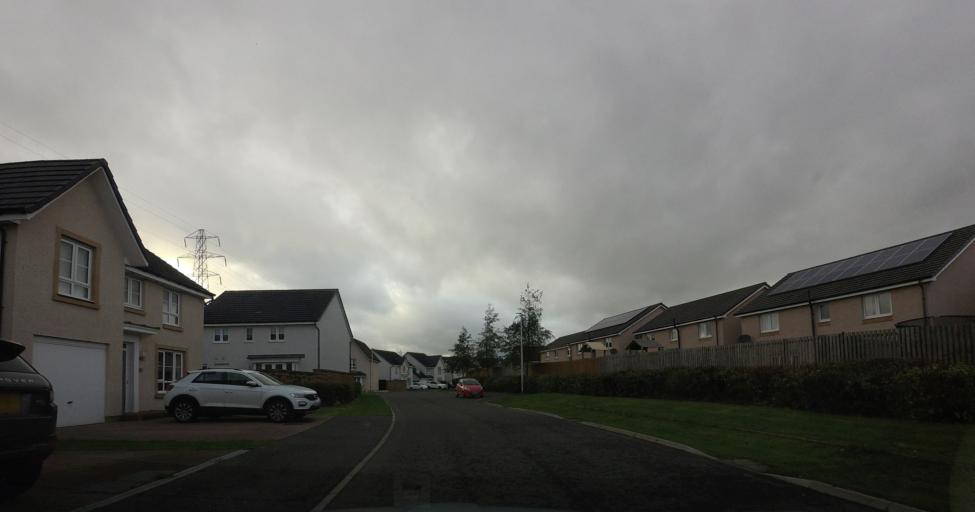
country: GB
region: Scotland
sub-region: West Lothian
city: Bathgate
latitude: 55.8856
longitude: -3.6472
